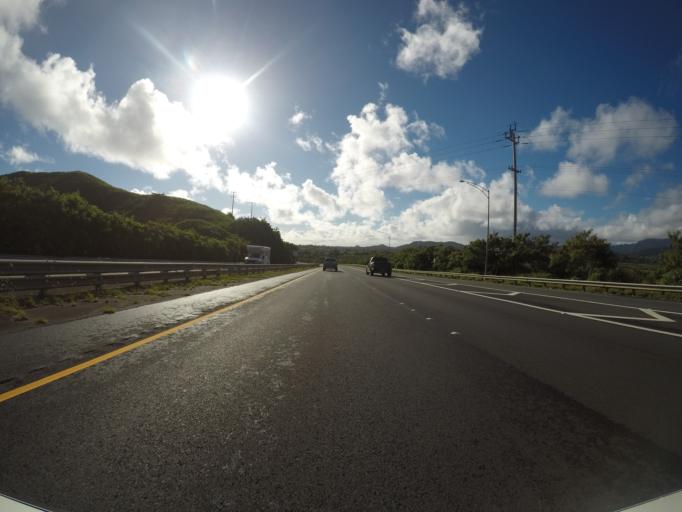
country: US
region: Hawaii
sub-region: Honolulu County
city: Kailua
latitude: 21.4061
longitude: -157.7637
